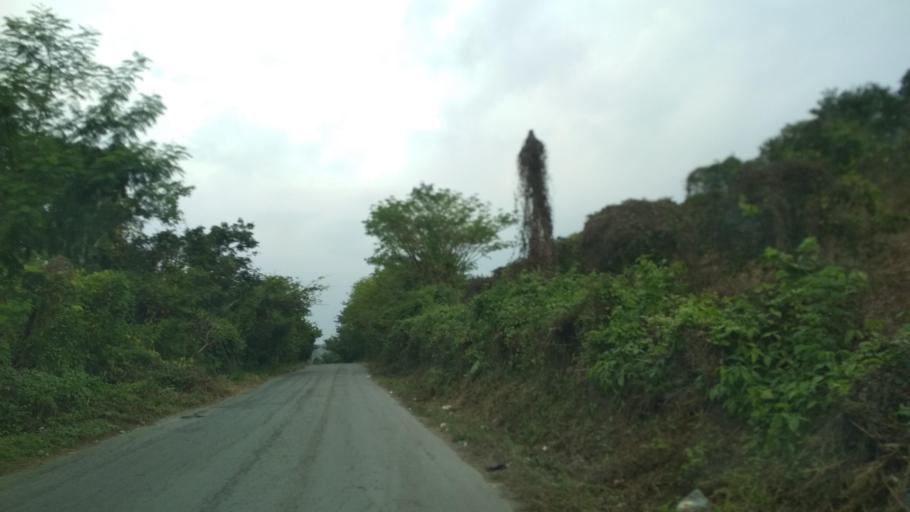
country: MM
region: Kayah
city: Loikaw
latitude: 20.2418
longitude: 97.2744
